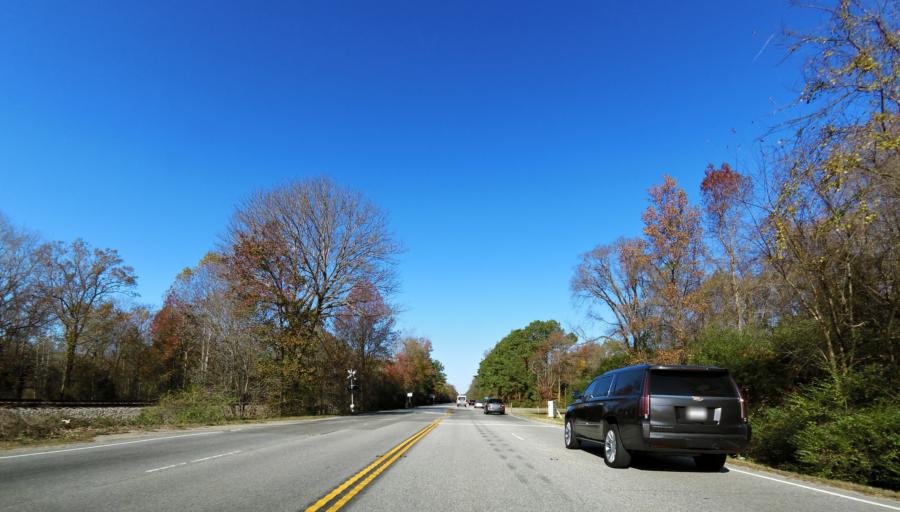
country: US
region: Virginia
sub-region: York County
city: Yorktown
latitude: 37.2228
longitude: -76.6135
